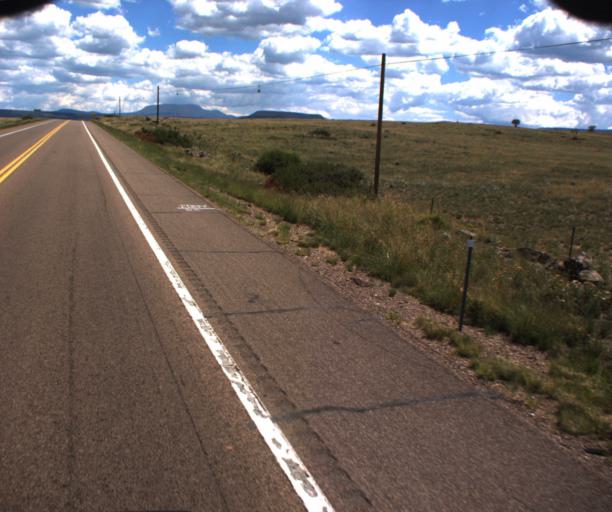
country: US
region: Arizona
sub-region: Apache County
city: Springerville
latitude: 34.1714
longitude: -109.3151
